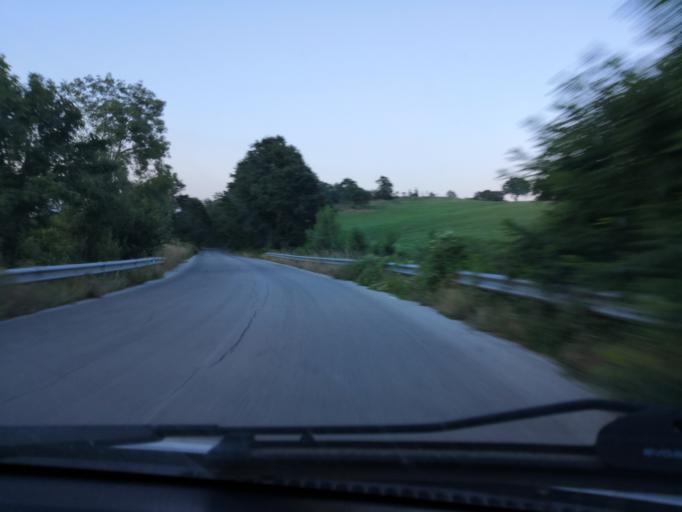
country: IT
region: Molise
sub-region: Provincia di Campobasso
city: Jelsi
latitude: 41.5097
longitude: 14.7758
